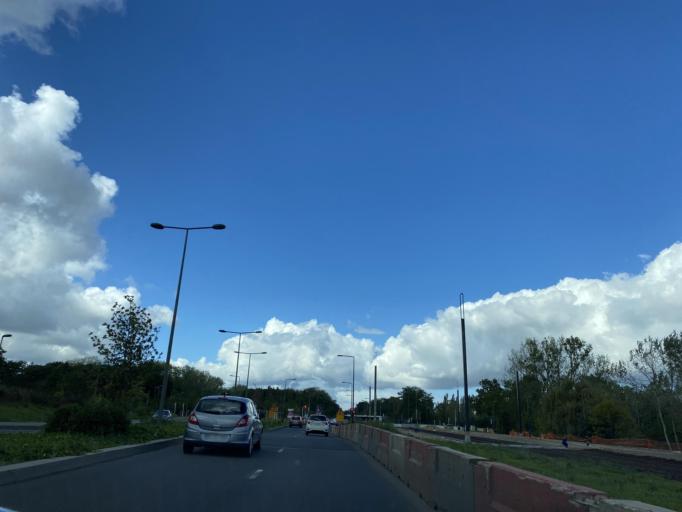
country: FR
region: Ile-de-France
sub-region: Departement de l'Essonne
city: Courcouronnes
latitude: 48.6246
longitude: 2.4081
